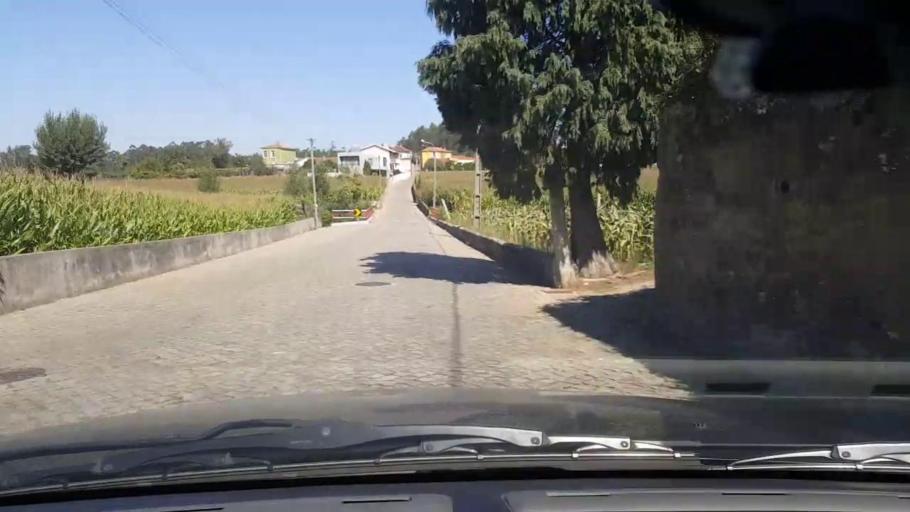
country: PT
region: Porto
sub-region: Matosinhos
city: Lavra
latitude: 41.2705
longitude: -8.6948
